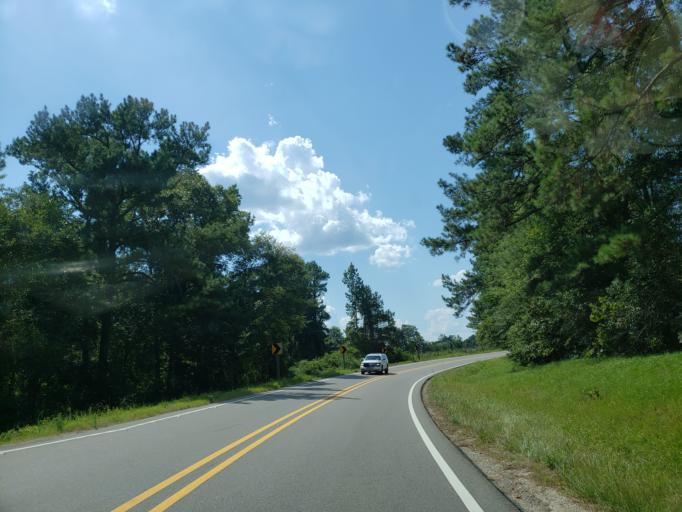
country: US
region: Mississippi
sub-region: Lamar County
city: Sumrall
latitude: 31.3681
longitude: -89.5078
